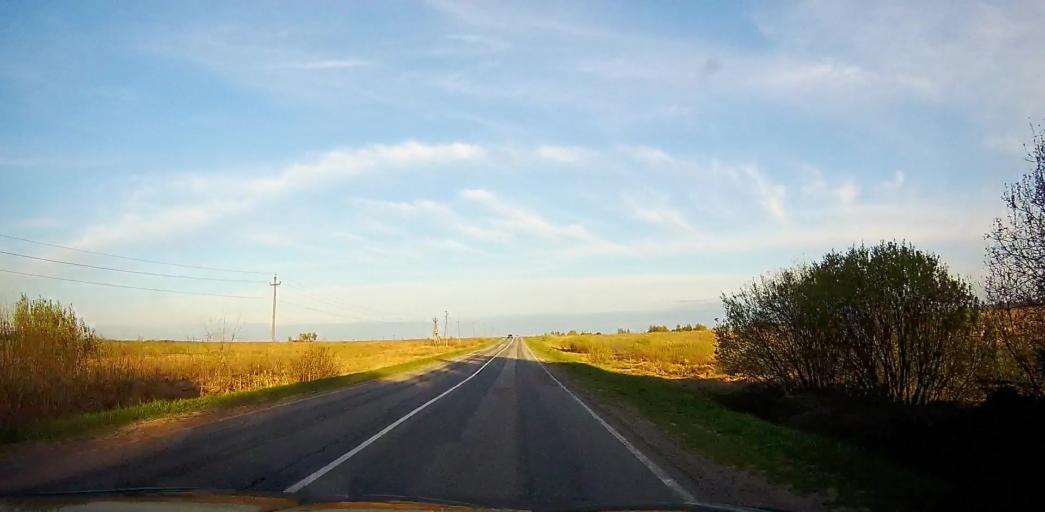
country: RU
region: Moskovskaya
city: Bronnitsy
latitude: 55.2744
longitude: 38.2286
